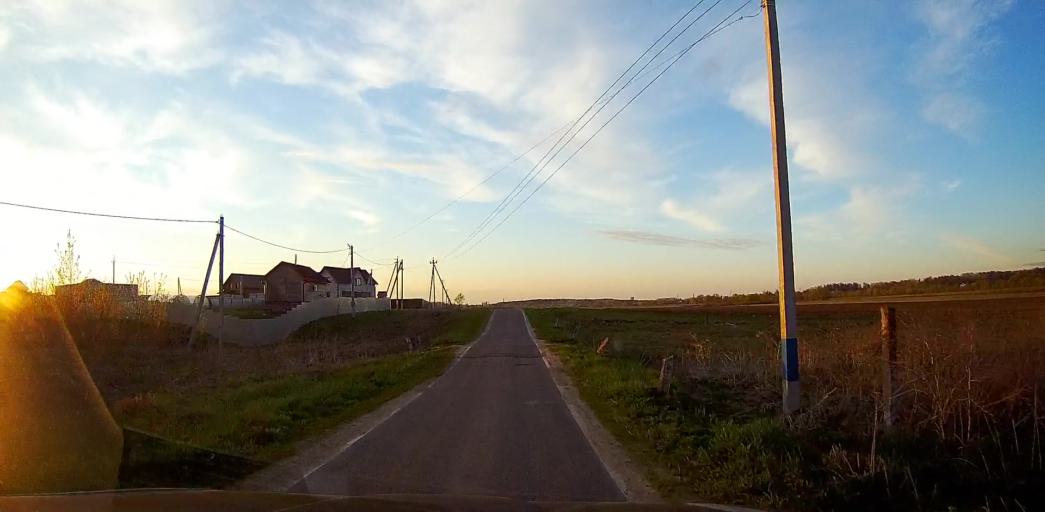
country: RU
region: Moskovskaya
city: Peski
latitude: 55.2133
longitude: 38.7392
